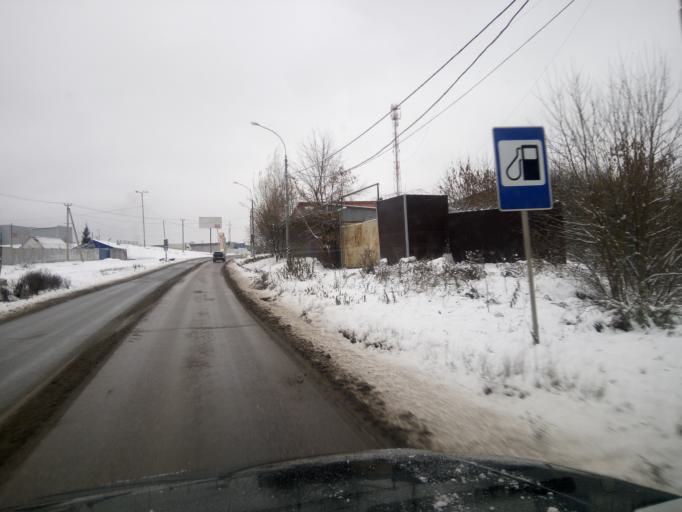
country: RU
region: Moskovskaya
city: Skhodnya
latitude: 55.9687
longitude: 37.3100
